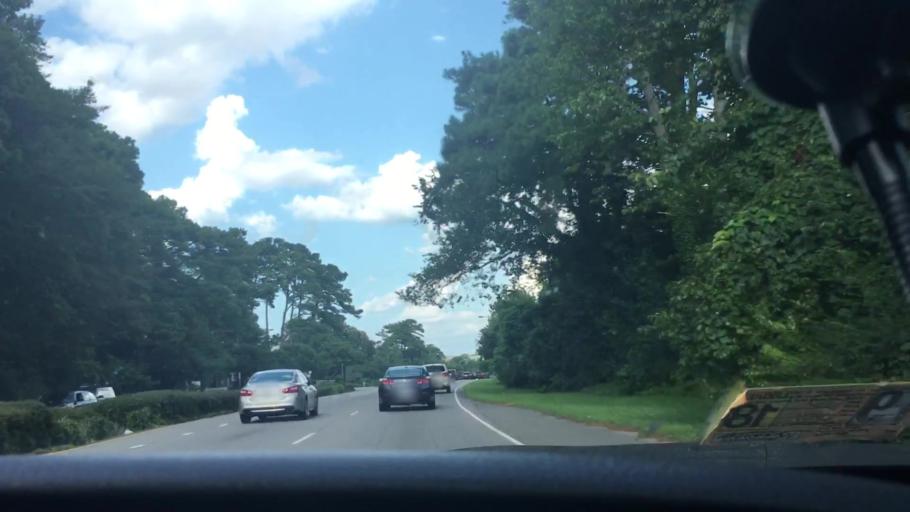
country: US
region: Virginia
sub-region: City of Virginia Beach
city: Virginia Beach
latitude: 36.9068
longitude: -76.1134
